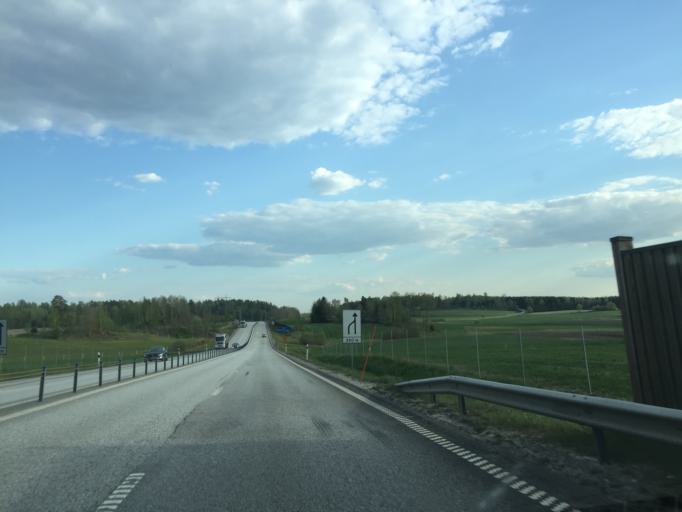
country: SE
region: OErebro
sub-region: Orebro Kommun
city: Hovsta
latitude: 59.3758
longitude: 15.2190
